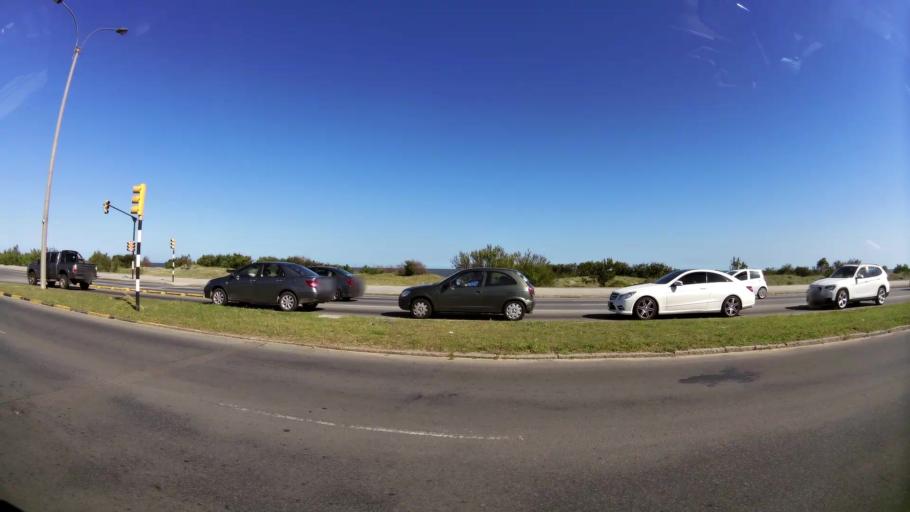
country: UY
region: Canelones
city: Barra de Carrasco
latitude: -34.8822
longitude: -56.0356
